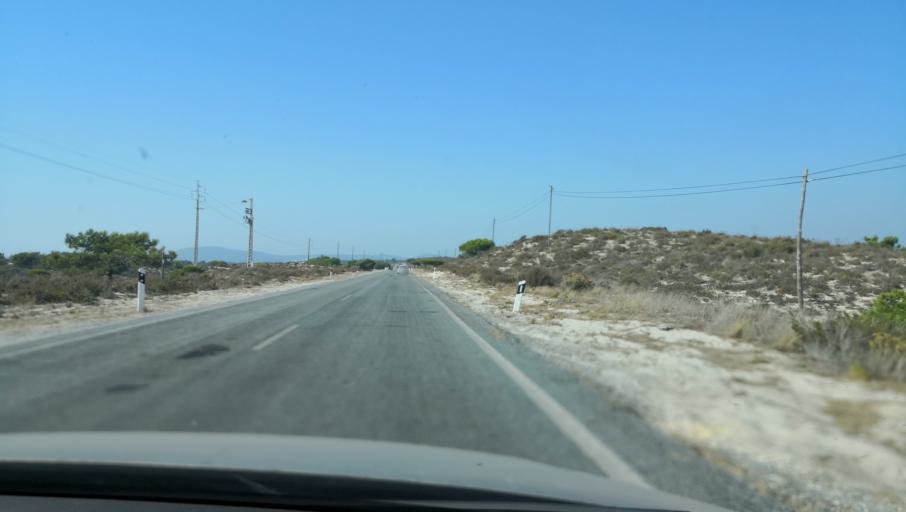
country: PT
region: Setubal
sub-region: Setubal
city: Setubal
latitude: 38.4235
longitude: -8.8225
